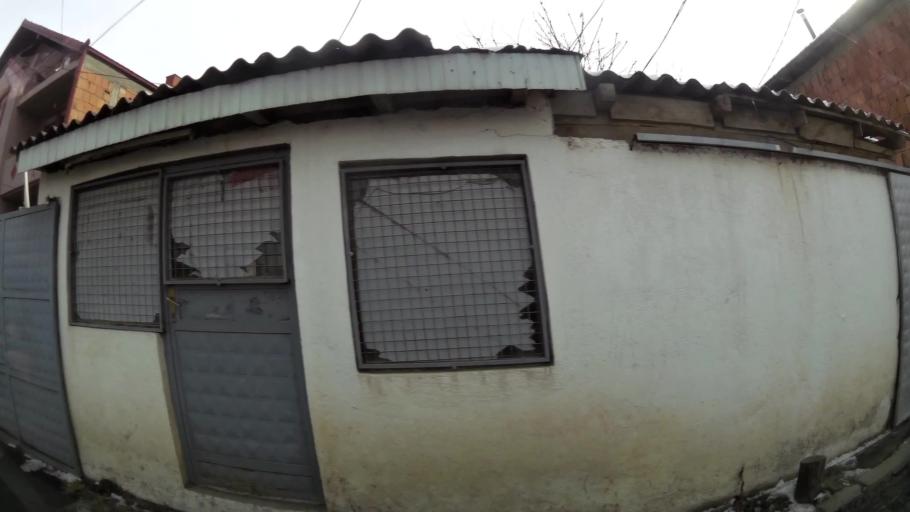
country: MK
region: Cair
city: Cair
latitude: 42.0094
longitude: 21.4375
